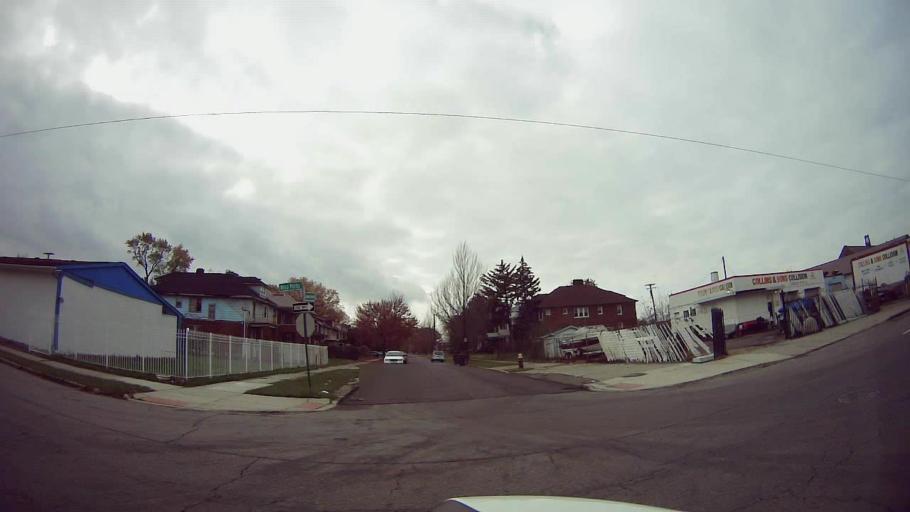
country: US
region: Michigan
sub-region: Wayne County
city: Highland Park
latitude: 42.3845
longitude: -83.1050
